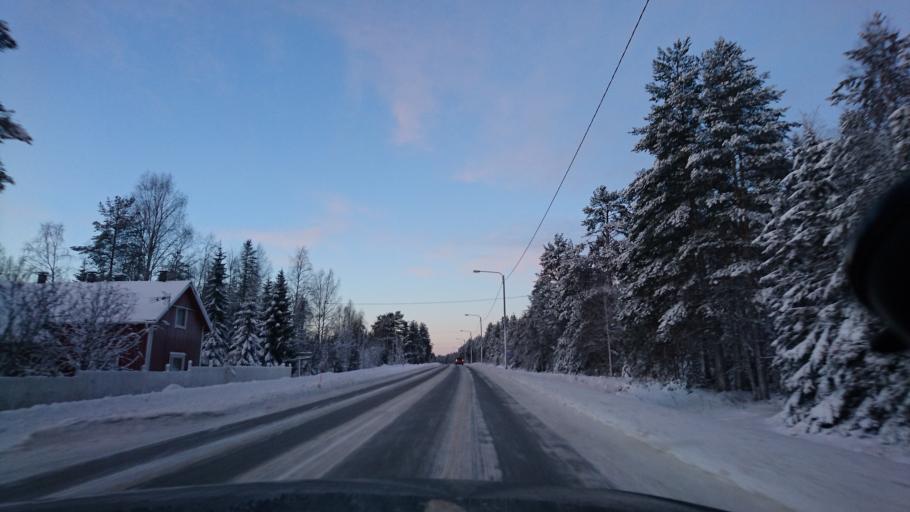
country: FI
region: Lapland
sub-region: Rovaniemi
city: Ranua
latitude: 65.9391
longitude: 26.4848
